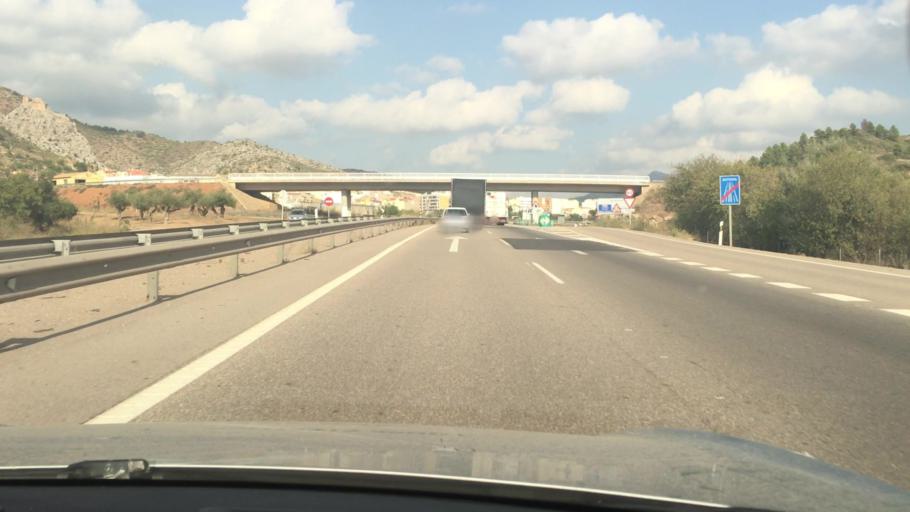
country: ES
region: Valencia
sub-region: Provincia de Castello
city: Borriol
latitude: 40.0343
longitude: -0.0791
